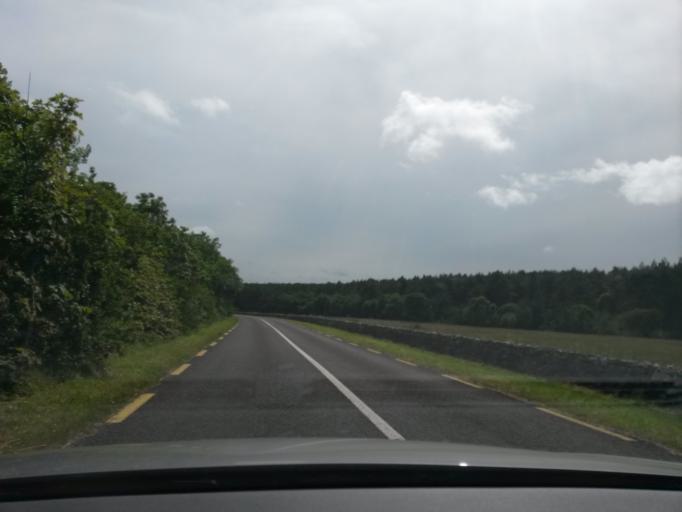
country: IE
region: Connaught
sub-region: County Leitrim
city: Kinlough
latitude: 54.4499
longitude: -8.4536
